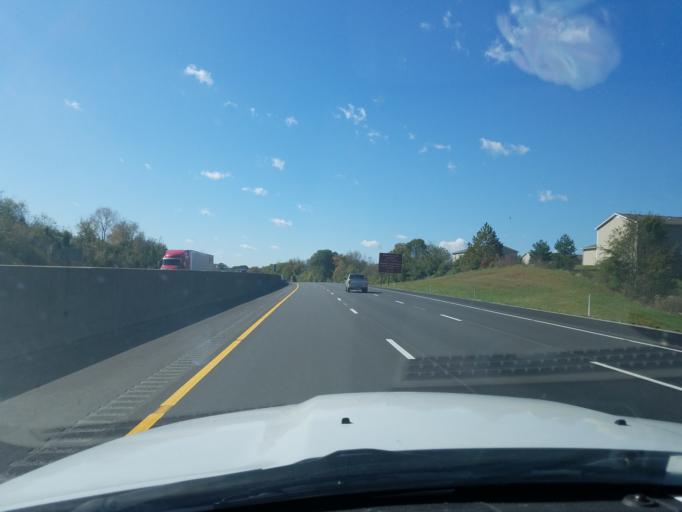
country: US
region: Kentucky
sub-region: Warren County
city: Bowling Green
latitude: 36.9948
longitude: -86.3809
